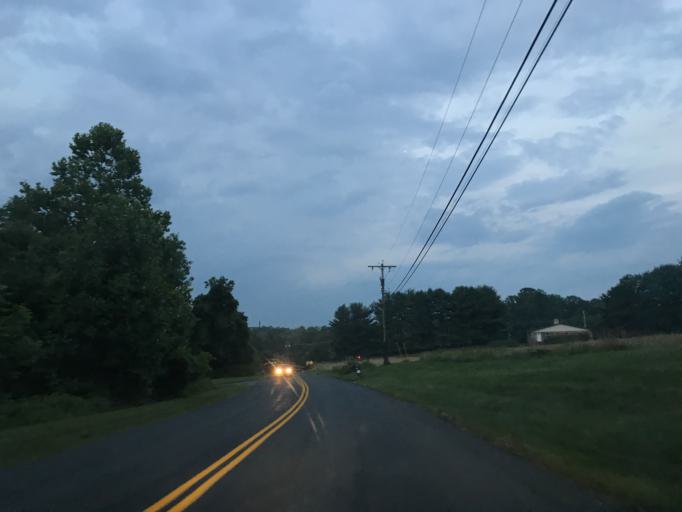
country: US
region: Maryland
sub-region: Harford County
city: Pleasant Hills
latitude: 39.4829
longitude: -76.4064
